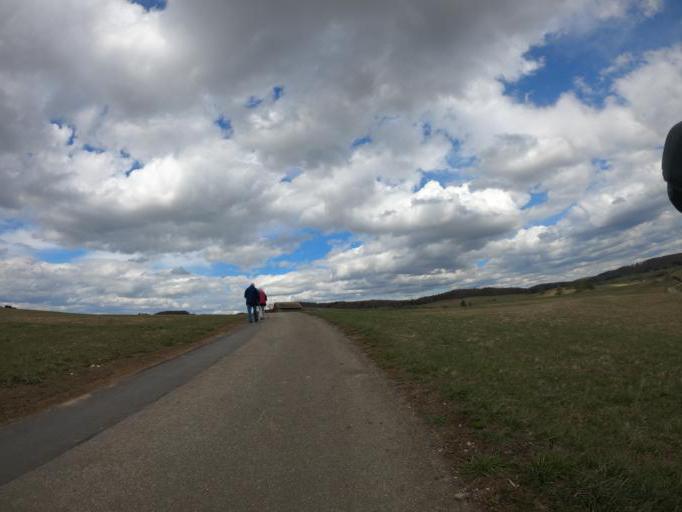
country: DE
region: Baden-Wuerttemberg
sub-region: Tuebingen Region
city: Pfullingen
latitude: 48.3869
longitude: 9.1970
